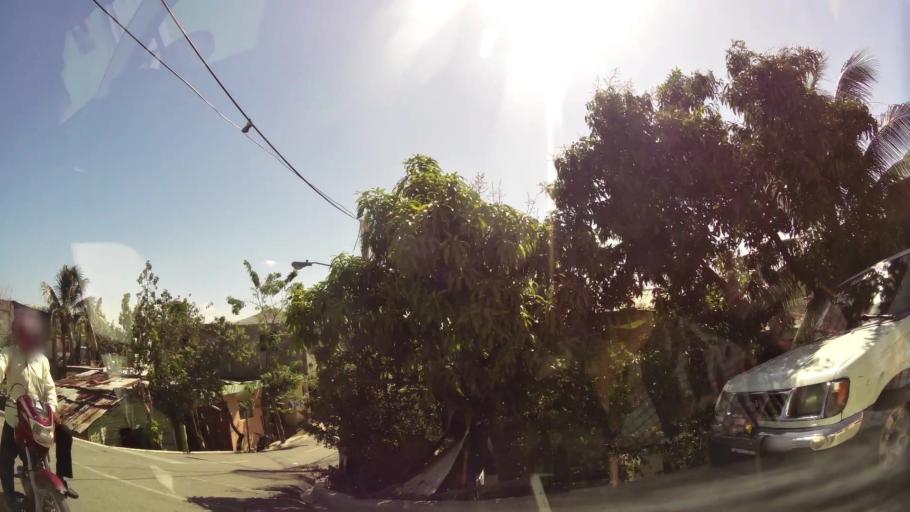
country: DO
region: San Cristobal
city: San Cristobal
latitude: 18.4269
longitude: -70.1327
